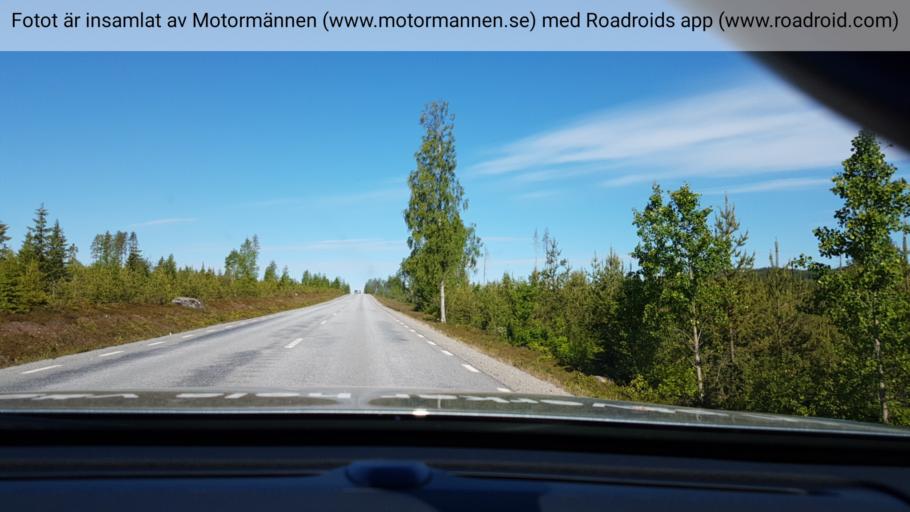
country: SE
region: Vaesterbotten
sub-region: Bjurholms Kommun
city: Bjurholm
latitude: 63.9506
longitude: 18.8949
